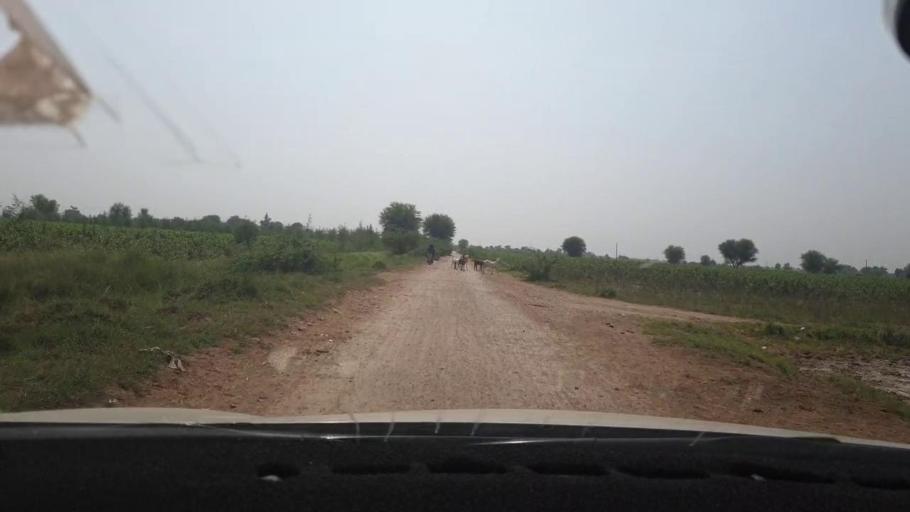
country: PK
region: Sindh
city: Tando Mittha Khan
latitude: 25.9336
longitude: 69.2247
